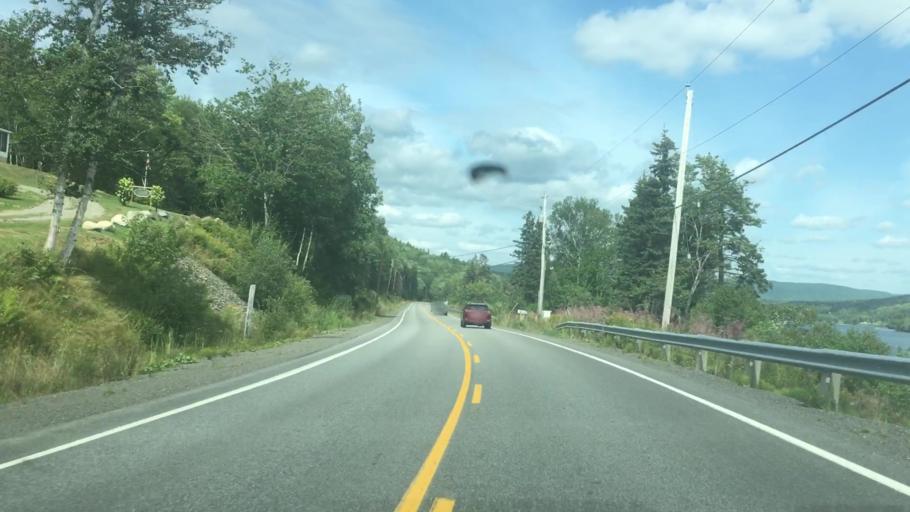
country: CA
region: Nova Scotia
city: Sydney Mines
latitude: 46.2728
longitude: -60.6098
